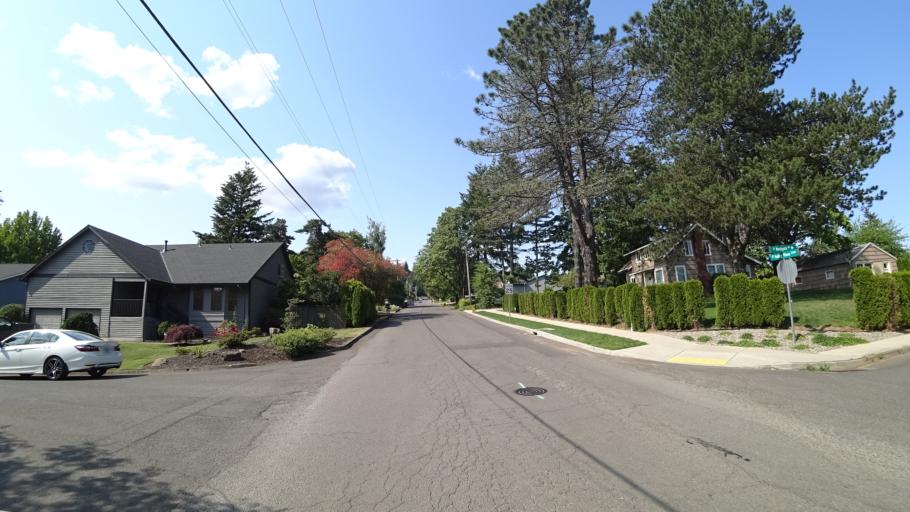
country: US
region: Oregon
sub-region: Clackamas County
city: Happy Valley
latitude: 45.4358
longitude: -122.5482
